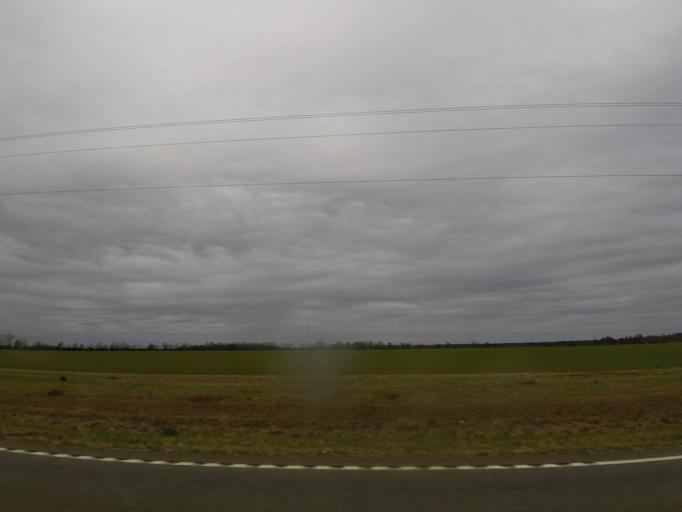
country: US
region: Georgia
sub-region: Randolph County
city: Shellman
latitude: 31.7721
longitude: -84.6280
